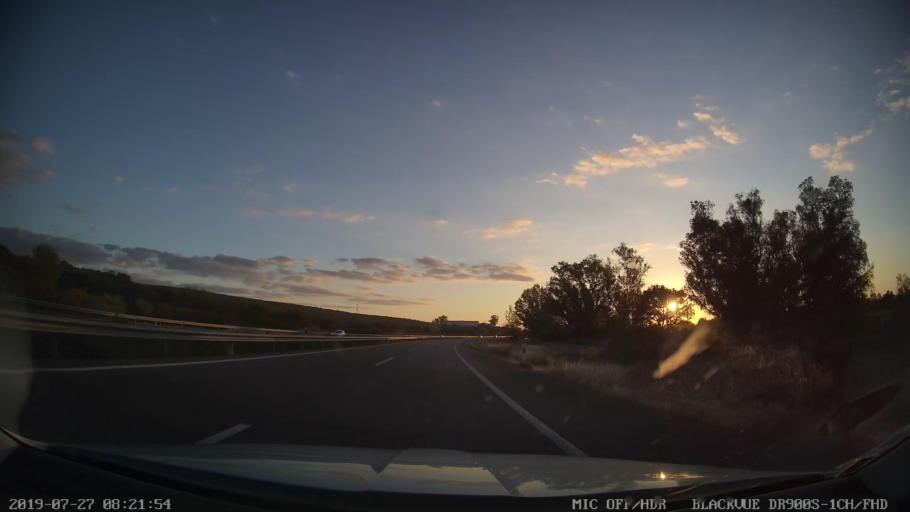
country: ES
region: Extremadura
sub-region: Provincia de Badajoz
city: Torremayor
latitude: 38.8604
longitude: -6.5344
